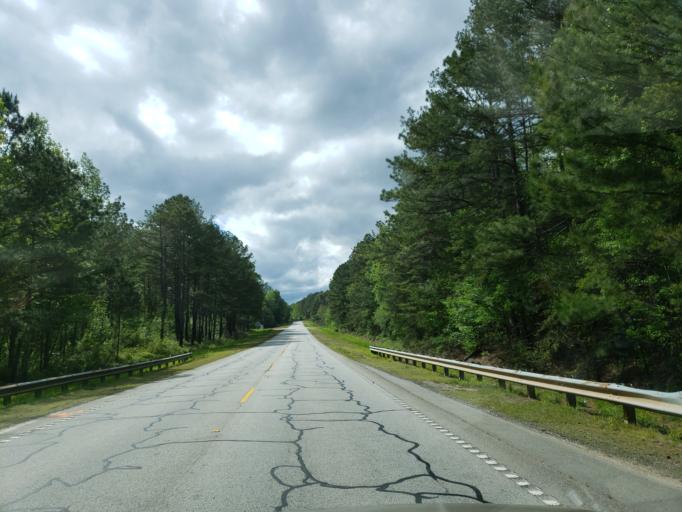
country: US
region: Georgia
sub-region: Haralson County
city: Tallapoosa
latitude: 33.7418
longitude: -85.3368
